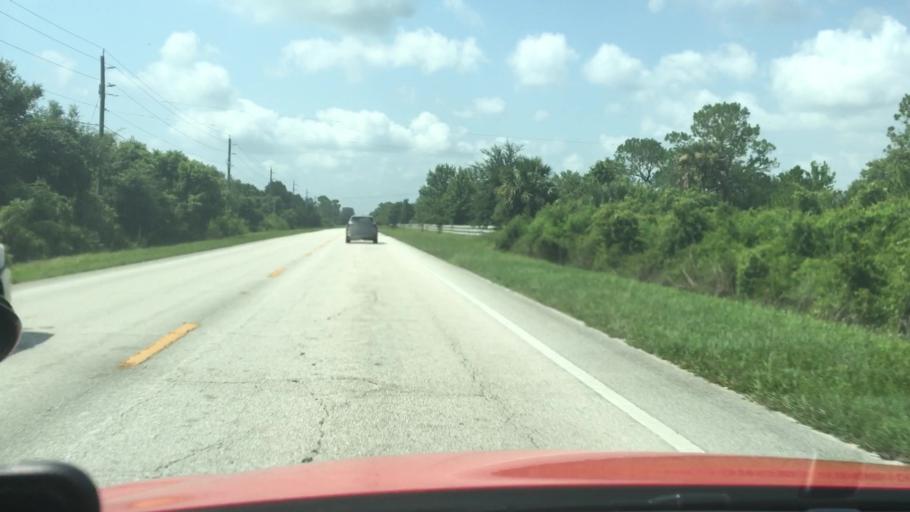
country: US
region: Florida
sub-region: Volusia County
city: Samsula-Spruce Creek
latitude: 29.0796
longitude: -81.0683
